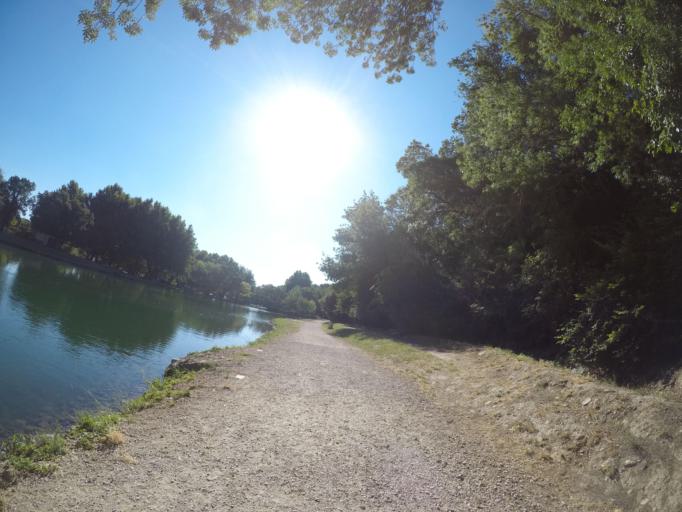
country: FR
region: Languedoc-Roussillon
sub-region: Departement des Pyrenees-Orientales
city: Le Soler
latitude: 42.6829
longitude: 2.7849
